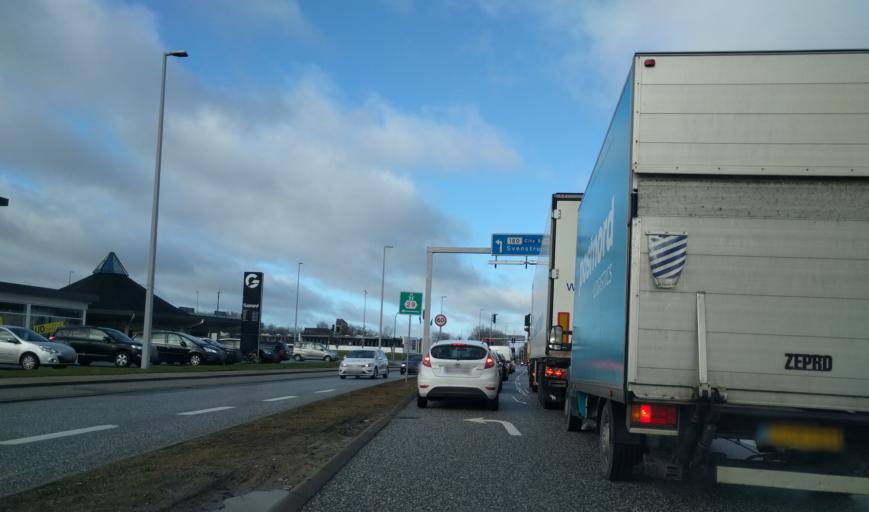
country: DK
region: North Denmark
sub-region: Alborg Kommune
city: Aalborg
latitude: 57.0142
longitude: 9.8944
